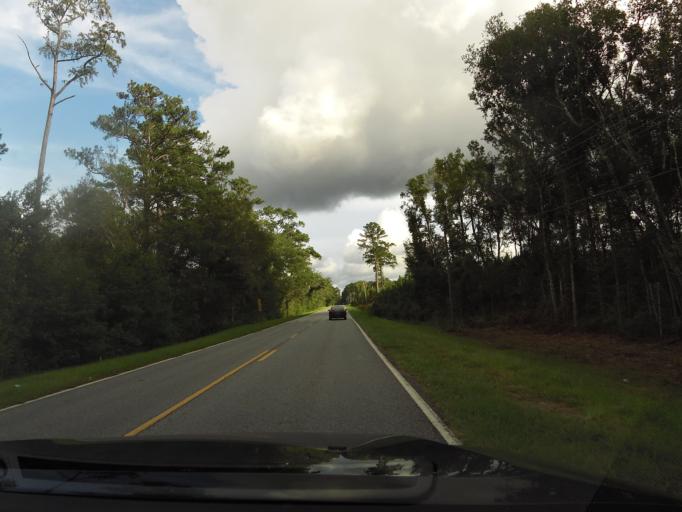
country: US
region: Georgia
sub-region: Liberty County
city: Midway
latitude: 31.8645
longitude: -81.4356
